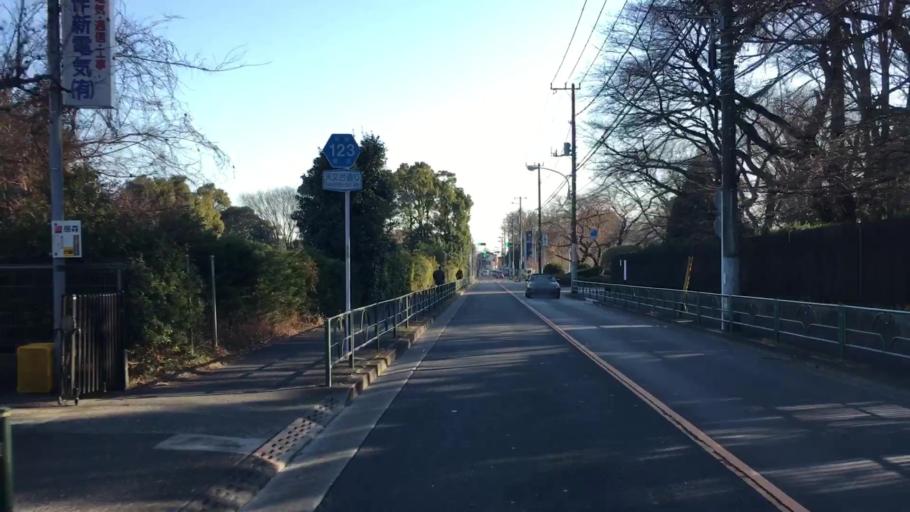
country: JP
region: Tokyo
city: Mitaka-shi
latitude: 35.6873
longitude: 139.5383
